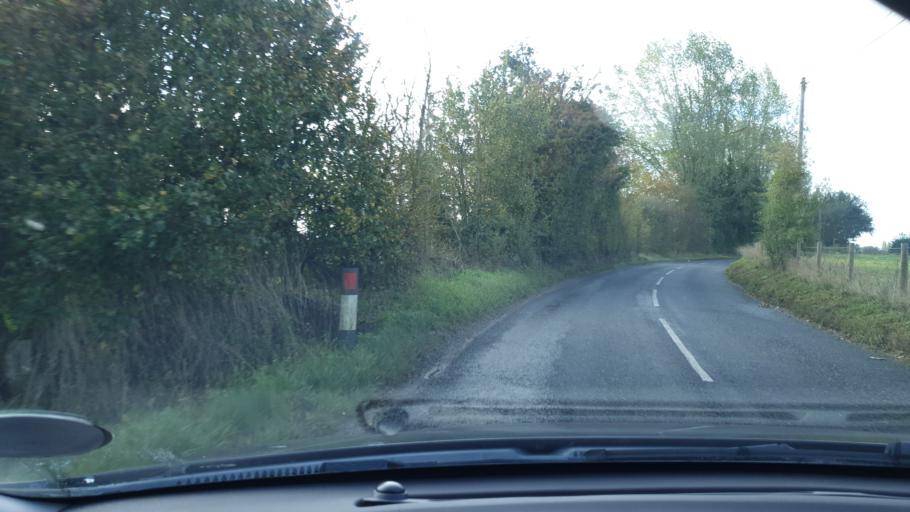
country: GB
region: England
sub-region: Essex
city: Manningtree
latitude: 51.9300
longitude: 1.0491
